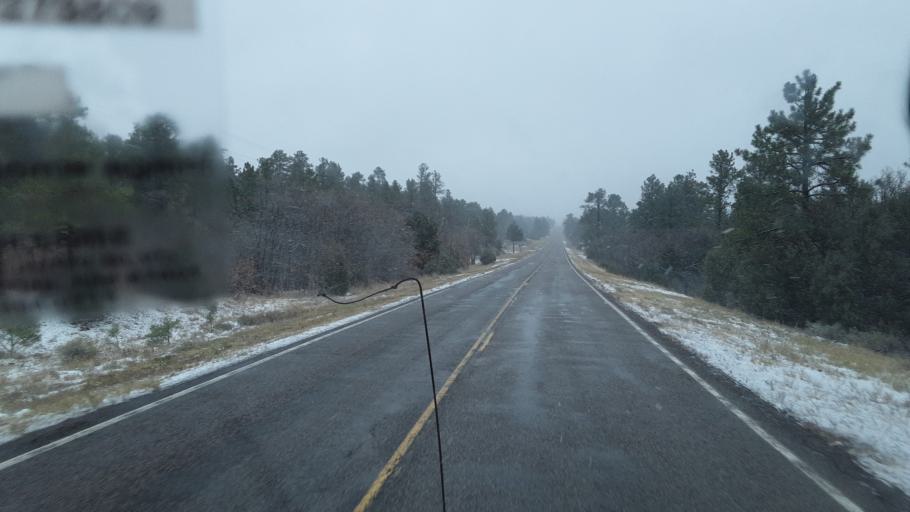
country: US
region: New Mexico
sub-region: Rio Arriba County
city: Tierra Amarilla
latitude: 36.6699
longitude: -106.5576
